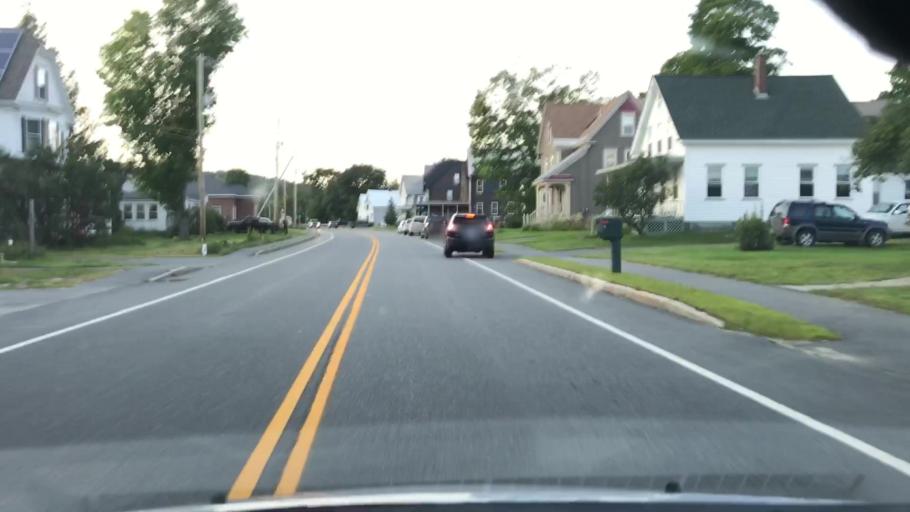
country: US
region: New Hampshire
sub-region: Grafton County
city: Rumney
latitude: 43.9178
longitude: -71.8884
